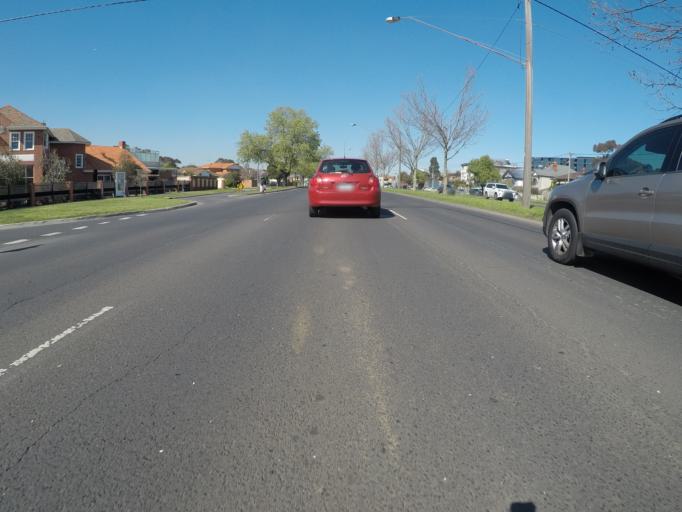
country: AU
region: Victoria
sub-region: Moonee Valley
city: Essendon North
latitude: -37.7415
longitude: 144.9084
